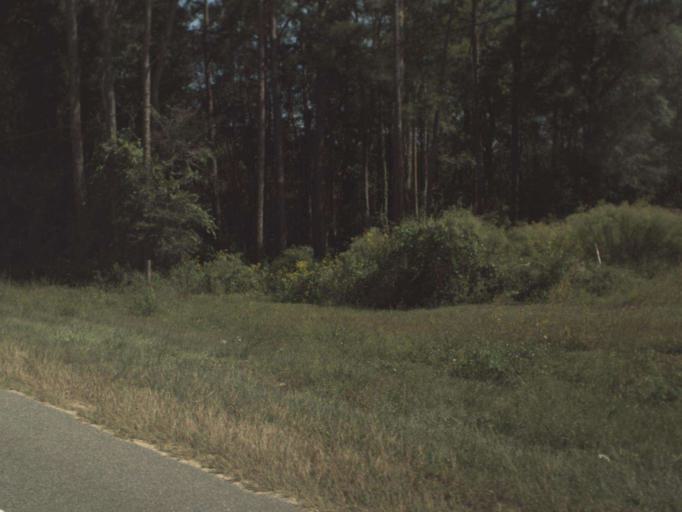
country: US
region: Florida
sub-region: Washington County
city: Chipley
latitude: 30.6619
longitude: -85.5775
